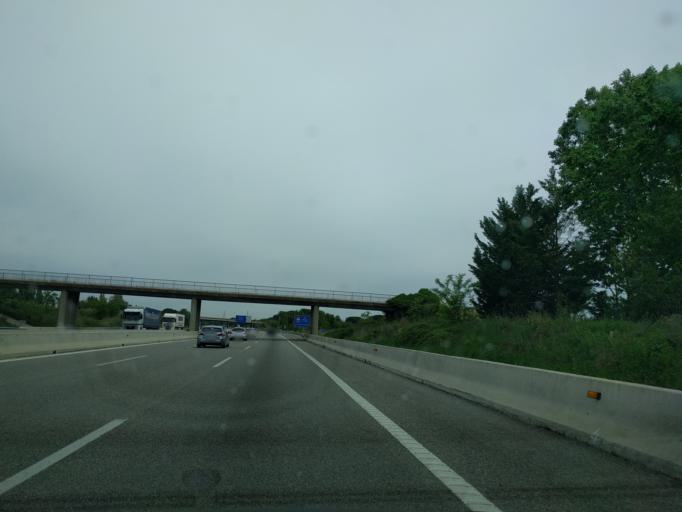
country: ES
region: Catalonia
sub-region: Provincia de Girona
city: Vilobi d'Onyar
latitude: 41.8880
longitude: 2.7741
